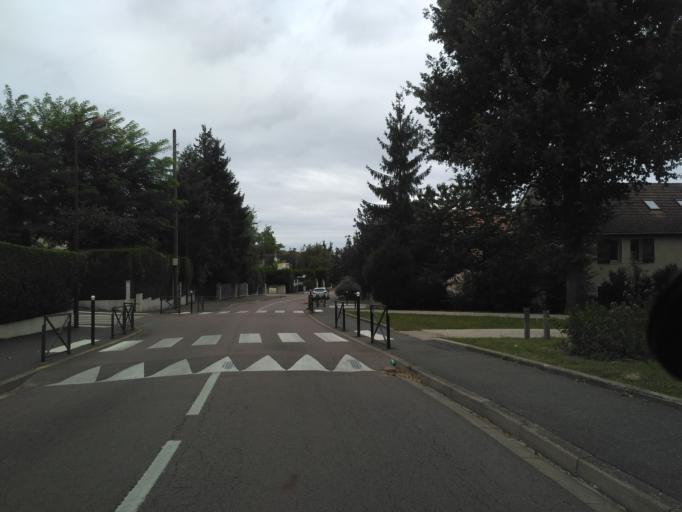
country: FR
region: Ile-de-France
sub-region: Departement de Seine-et-Marne
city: Cesson
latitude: 48.5622
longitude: 2.6133
